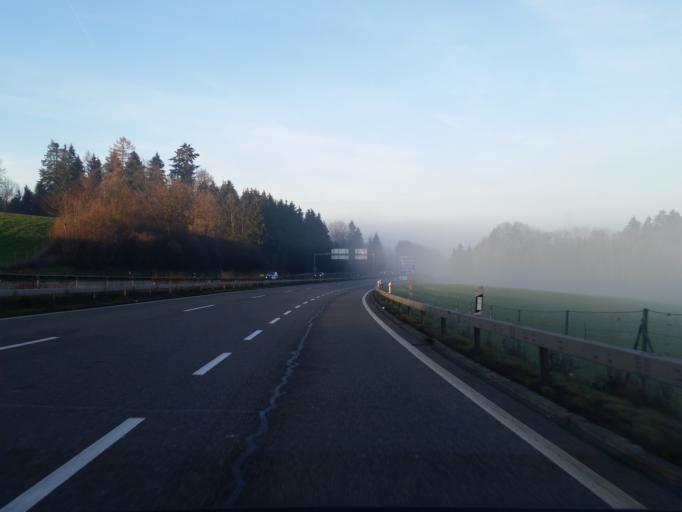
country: CH
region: Saint Gallen
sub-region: Wahlkreis Rorschach
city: Morschwil
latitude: 47.4741
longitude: 9.4420
